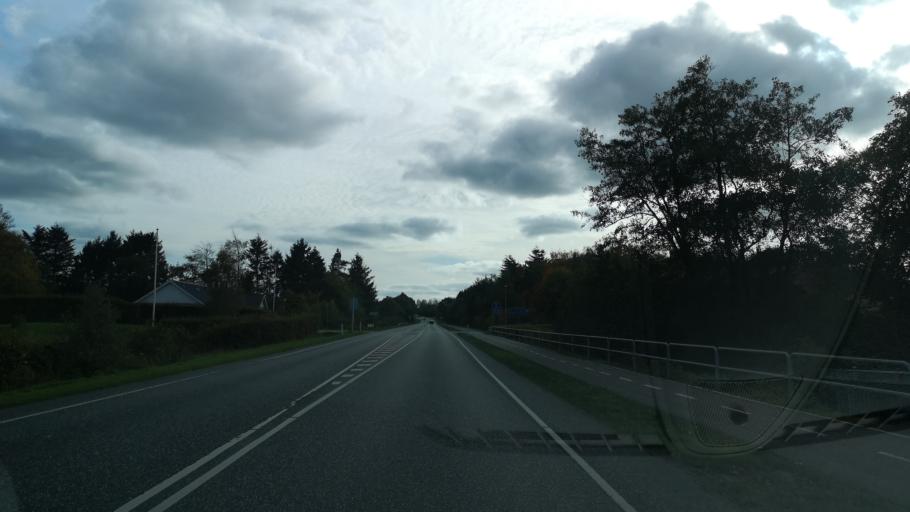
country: DK
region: Central Jutland
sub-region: Holstebro Kommune
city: Holstebro
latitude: 56.3401
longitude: 8.6124
